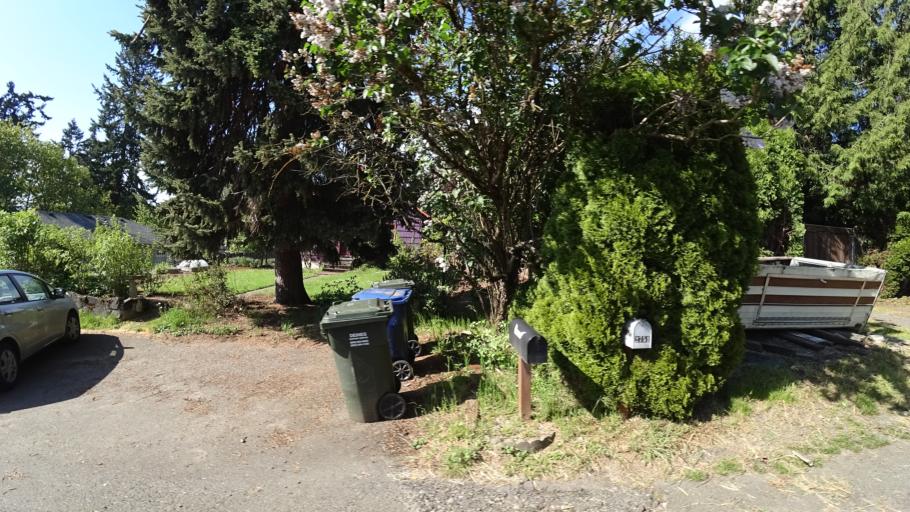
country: US
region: Oregon
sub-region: Clackamas County
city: Milwaukie
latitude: 45.4561
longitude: -122.6340
